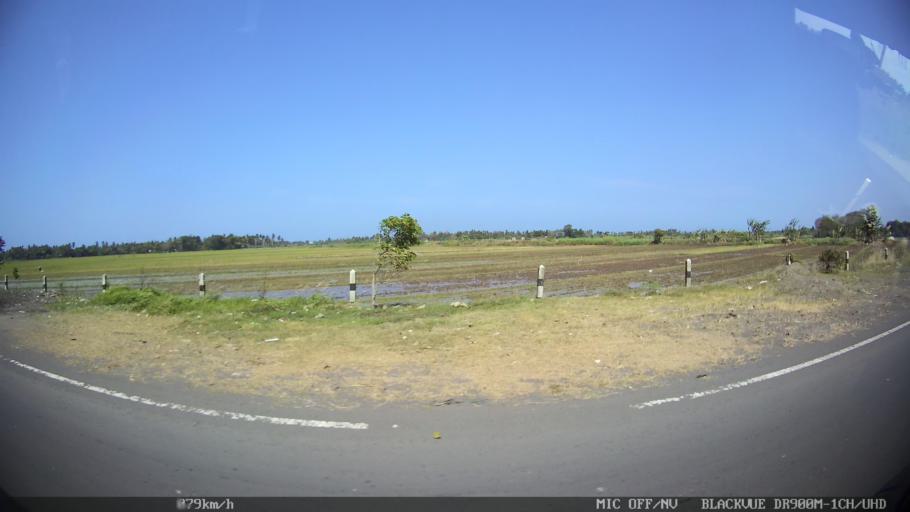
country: ID
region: Daerah Istimewa Yogyakarta
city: Srandakan
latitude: -7.9646
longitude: 110.2051
